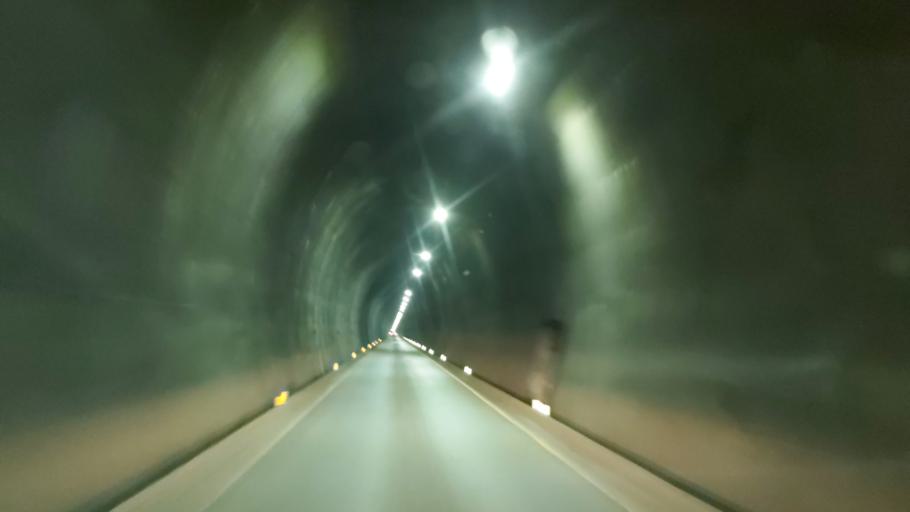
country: CL
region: Araucania
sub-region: Provincia de Cautin
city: Vilcun
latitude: -38.5458
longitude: -71.5038
